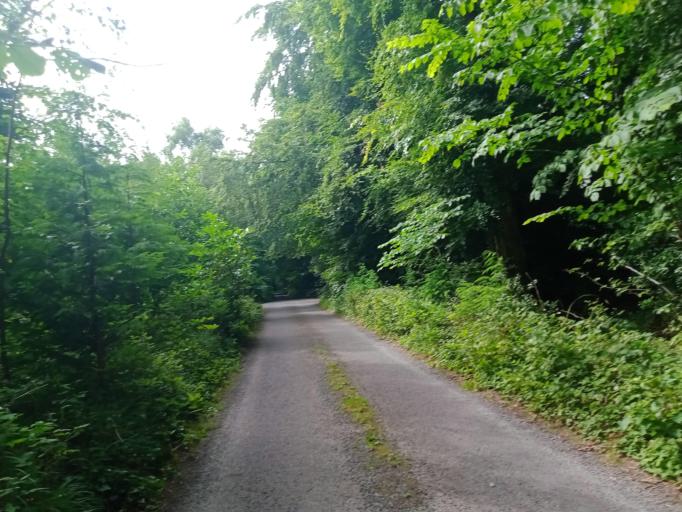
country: IE
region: Leinster
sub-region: Laois
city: Abbeyleix
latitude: 52.9007
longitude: -7.3612
